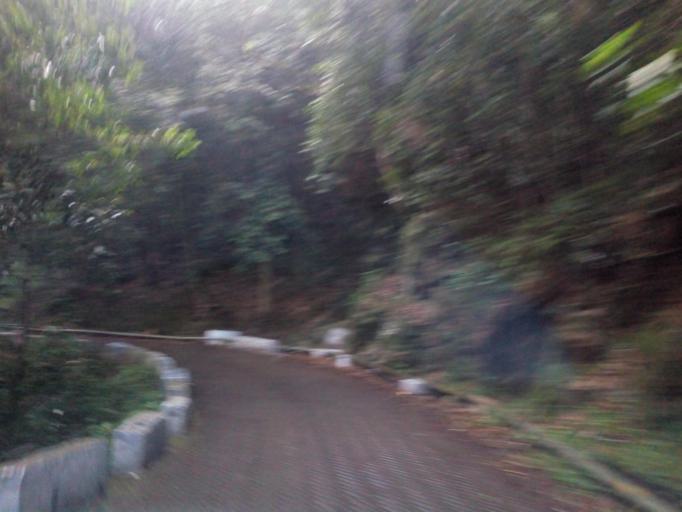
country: IN
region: Tamil Nadu
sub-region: Nilgiri
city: Wellington
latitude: 11.3510
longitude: 76.8247
